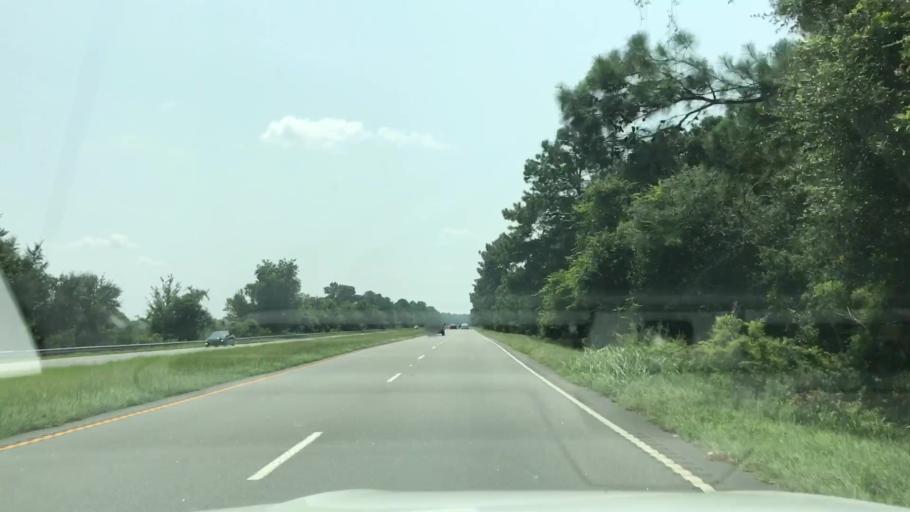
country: US
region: South Carolina
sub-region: Georgetown County
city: Georgetown
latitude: 33.1963
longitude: -79.3954
